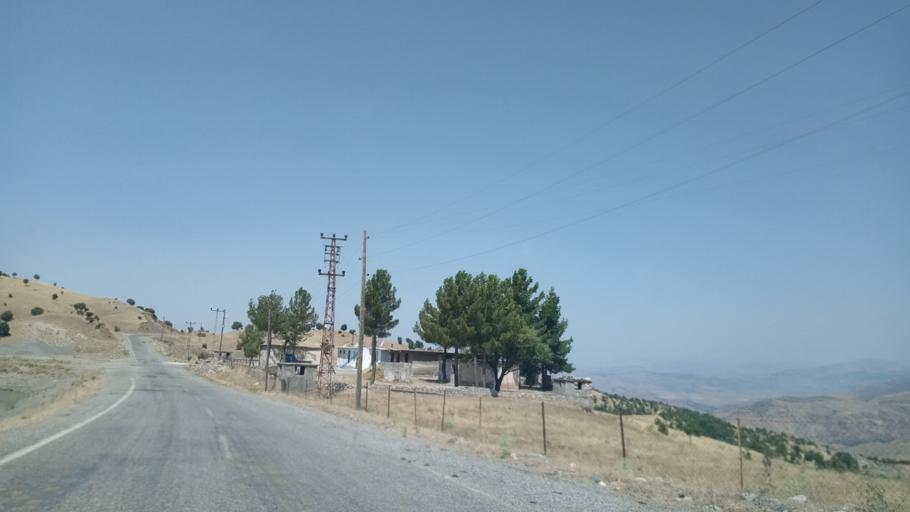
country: TR
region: Siirt
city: Dilektepe
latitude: 38.0765
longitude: 41.8236
